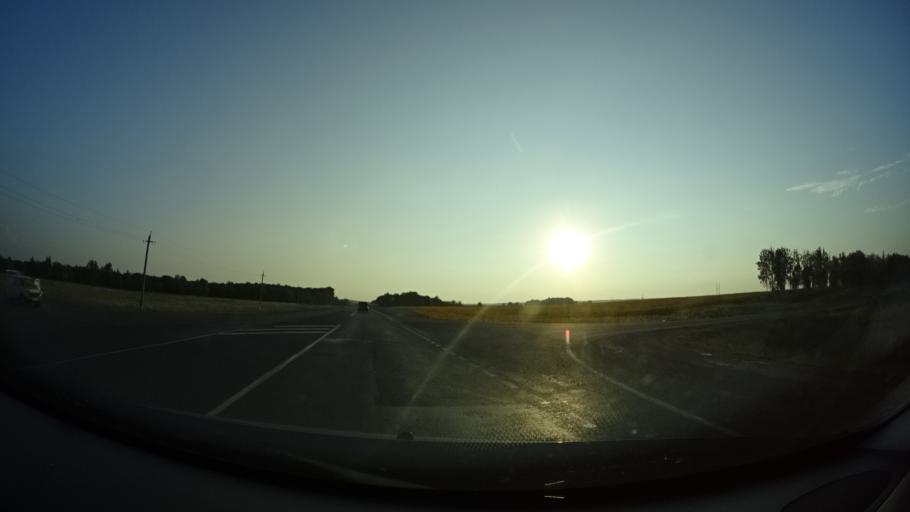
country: RU
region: Samara
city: Isakly
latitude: 54.0154
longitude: 51.7446
